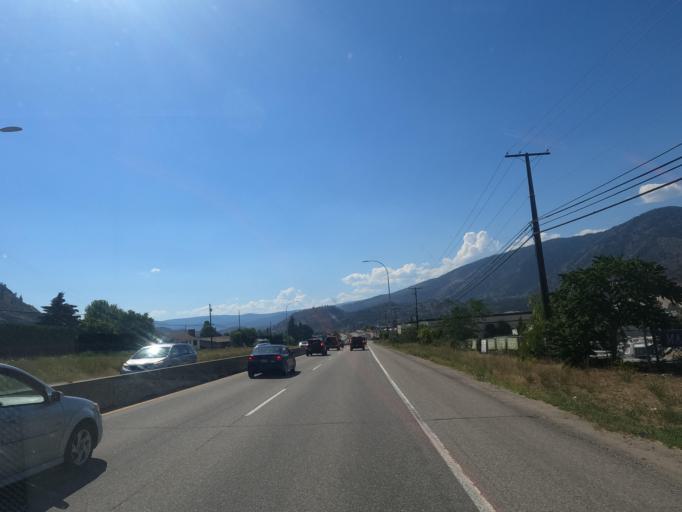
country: CA
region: British Columbia
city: West Kelowna
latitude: 49.8627
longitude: -119.5709
